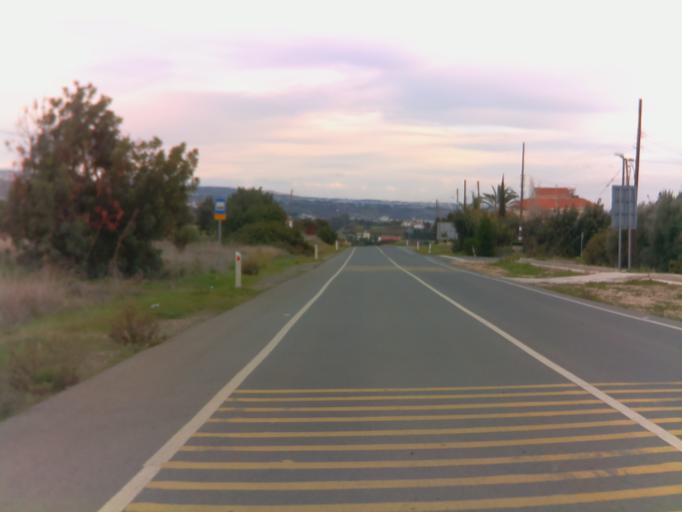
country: CY
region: Pafos
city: Pegeia
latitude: 34.8739
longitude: 32.3583
